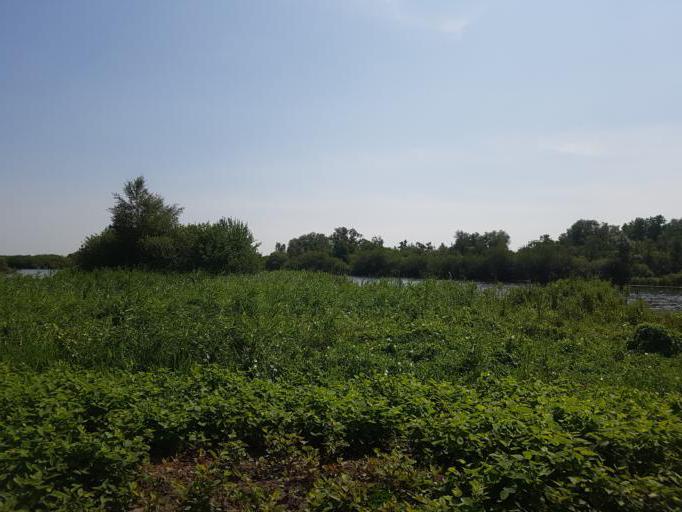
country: NL
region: Overijssel
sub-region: Gemeente Steenwijkerland
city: Giethoorn
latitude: 52.7674
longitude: 6.0876
